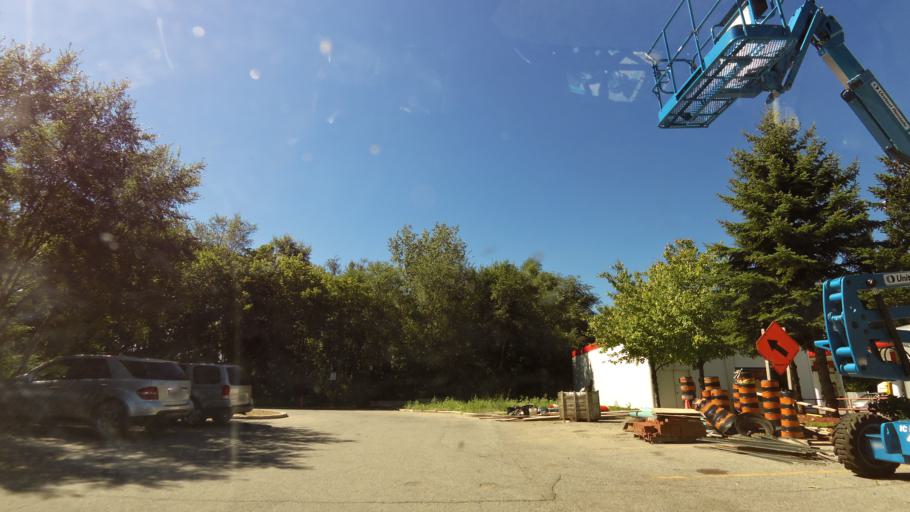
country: CA
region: Ontario
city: Toronto
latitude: 43.6362
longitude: -79.4748
